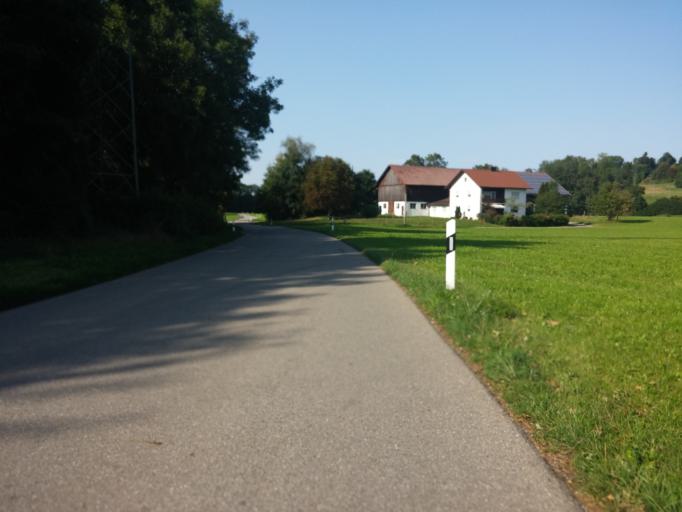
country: DE
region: Bavaria
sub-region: Swabia
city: Lautrach
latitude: 47.9086
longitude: 10.1241
